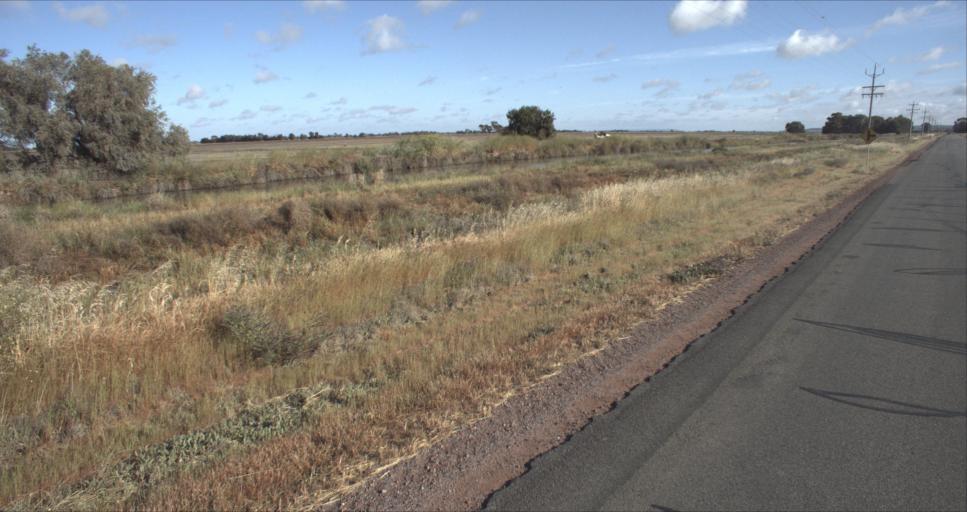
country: AU
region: New South Wales
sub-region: Leeton
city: Leeton
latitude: -34.5285
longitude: 146.3892
